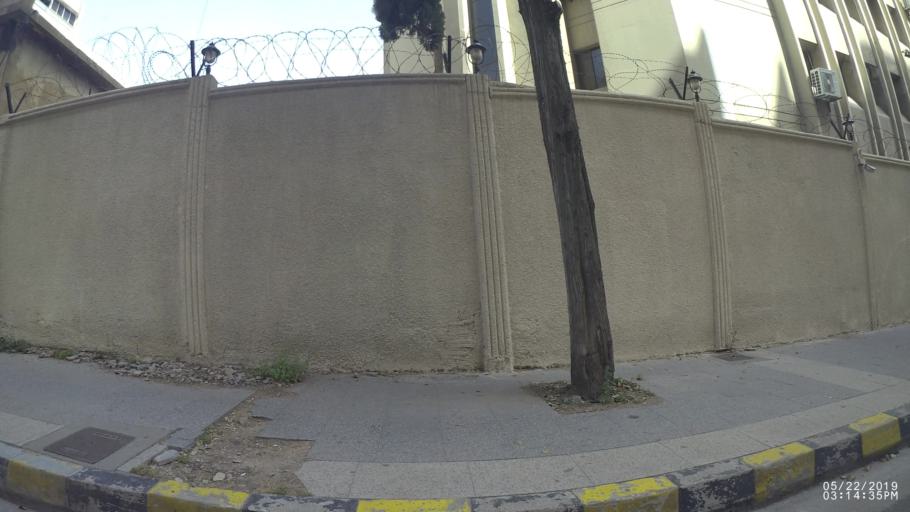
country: LB
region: Beyrouth
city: Beirut
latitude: 33.8818
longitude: 35.4910
